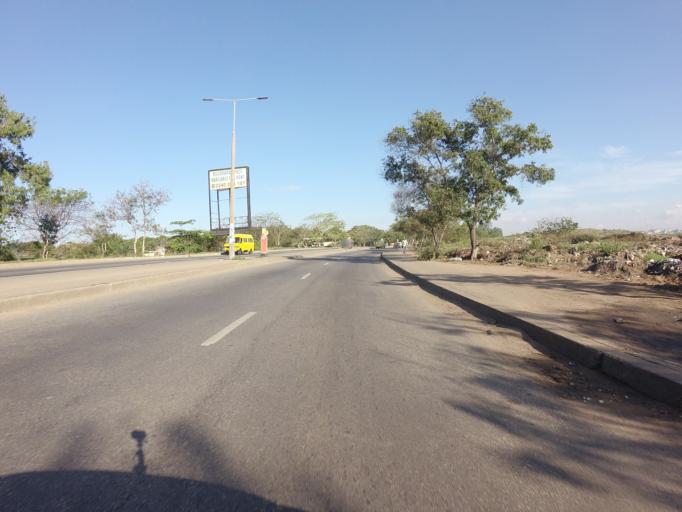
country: GH
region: Greater Accra
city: Accra
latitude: 5.5415
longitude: -0.2254
